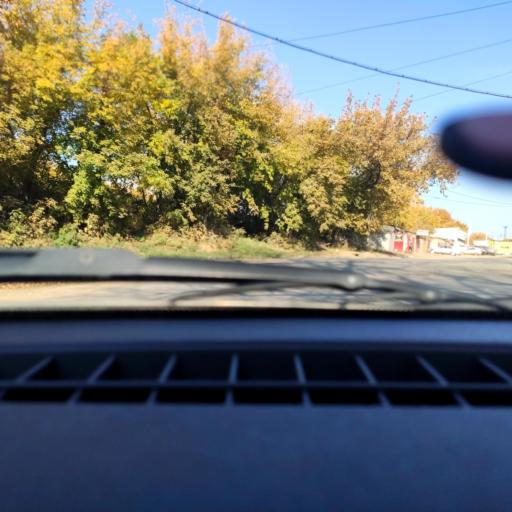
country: RU
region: Bashkortostan
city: Ufa
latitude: 54.8239
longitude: 56.0853
